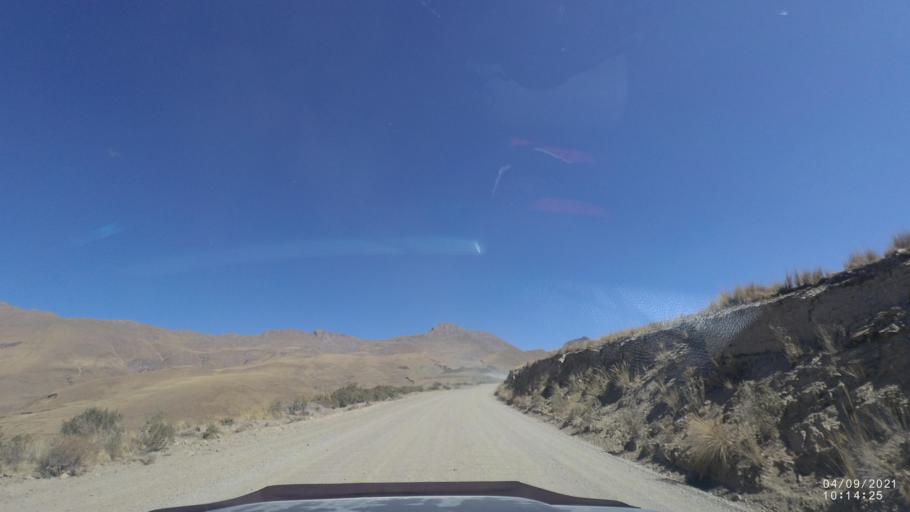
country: BO
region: Cochabamba
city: Sipe Sipe
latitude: -17.3300
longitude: -66.4085
